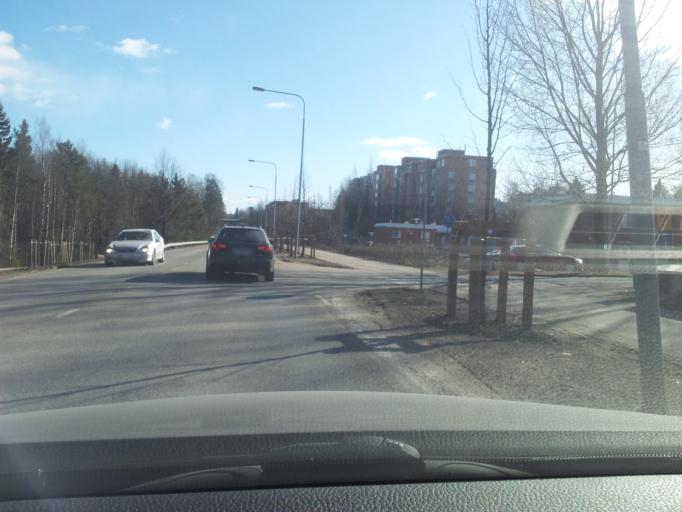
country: FI
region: Uusimaa
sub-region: Helsinki
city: Koukkuniemi
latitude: 60.1708
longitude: 24.7324
